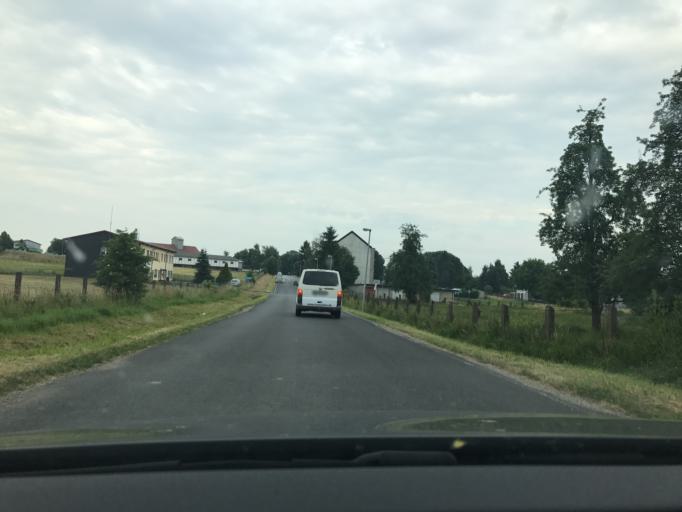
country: DE
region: Thuringia
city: Anrode
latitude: 51.2552
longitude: 10.3840
